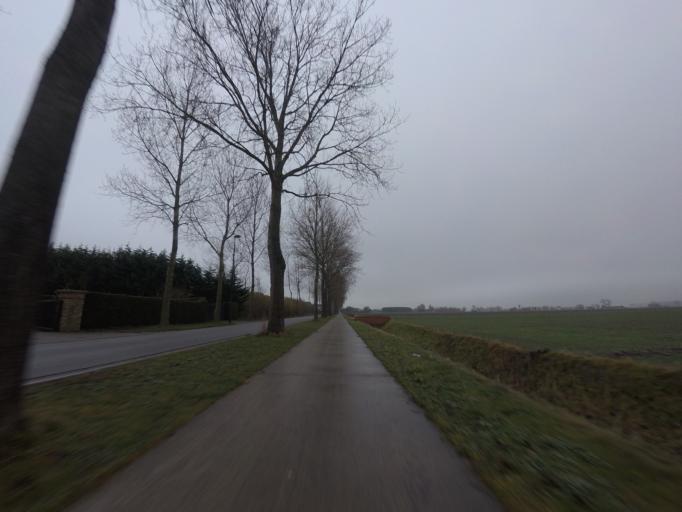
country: BE
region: Flanders
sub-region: Provincie West-Vlaanderen
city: Knokke-Heist
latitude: 51.3190
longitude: 3.2881
